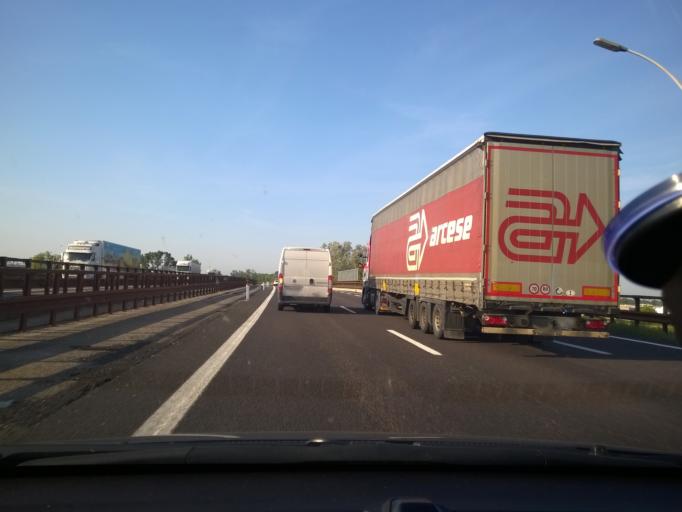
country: IT
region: Lombardy
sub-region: Provincia di Mantova
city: Bondeno
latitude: 44.9105
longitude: 10.8487
